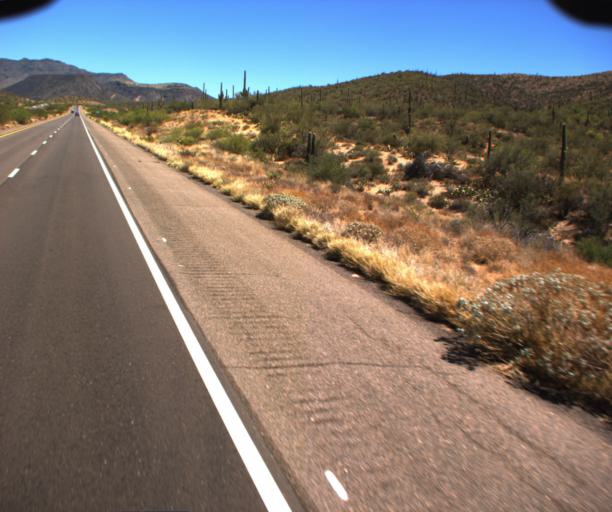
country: US
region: Arizona
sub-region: Maricopa County
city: Rio Verde
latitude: 33.7753
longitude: -111.4928
